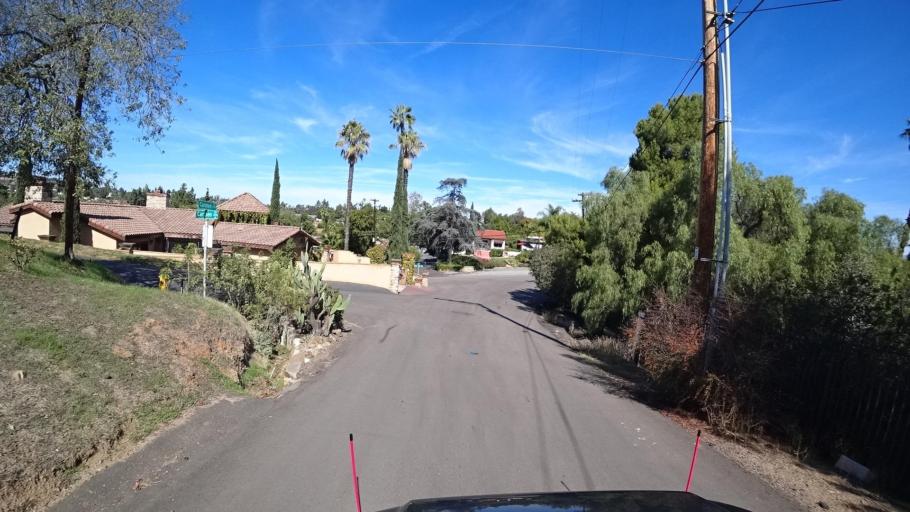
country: US
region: California
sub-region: San Diego County
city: Casa de Oro-Mount Helix
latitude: 32.7608
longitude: -116.9666
